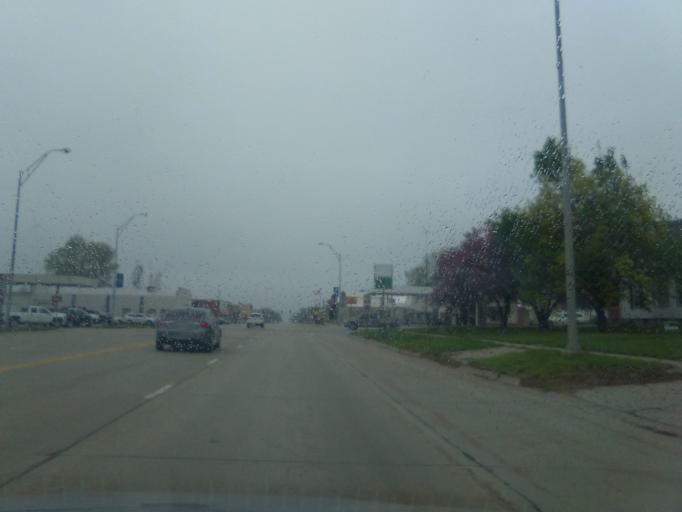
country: US
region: Nebraska
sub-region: Cuming County
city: Wisner
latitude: 41.9857
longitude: -96.9114
